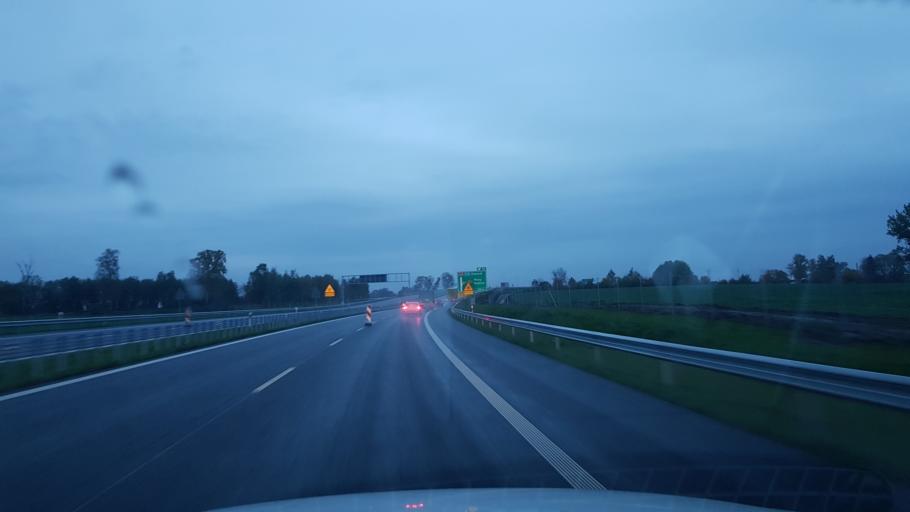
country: PL
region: West Pomeranian Voivodeship
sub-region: Powiat gryficki
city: Ploty
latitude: 53.8090
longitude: 15.2477
